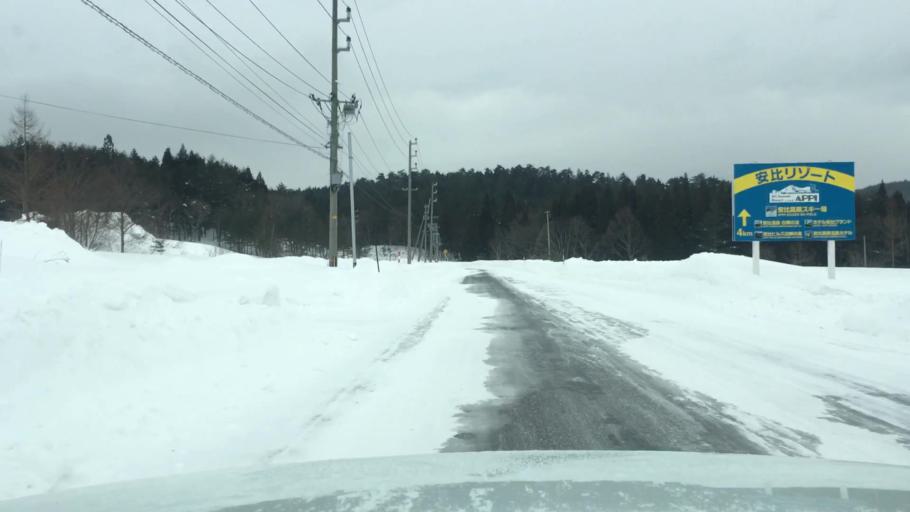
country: JP
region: Akita
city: Hanawa
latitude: 39.9928
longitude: 140.9957
